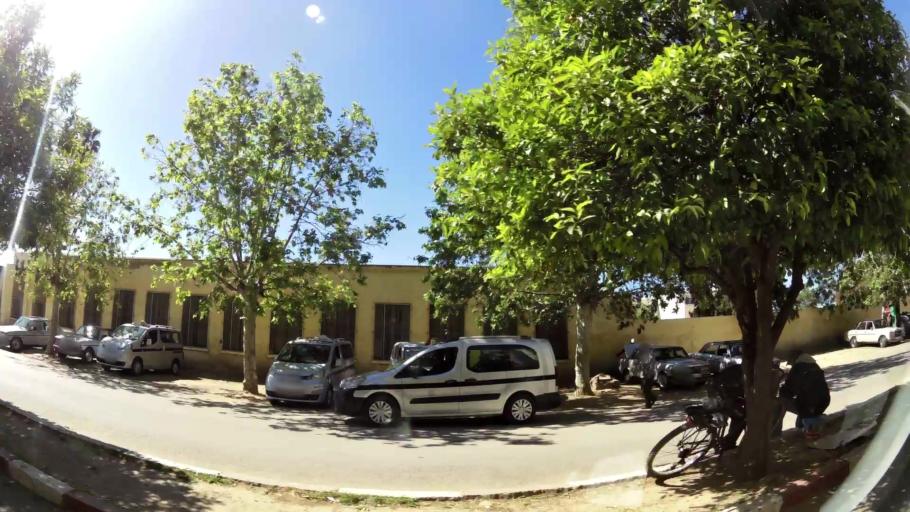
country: MA
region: Meknes-Tafilalet
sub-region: Meknes
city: Meknes
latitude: 33.8942
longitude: -5.5408
